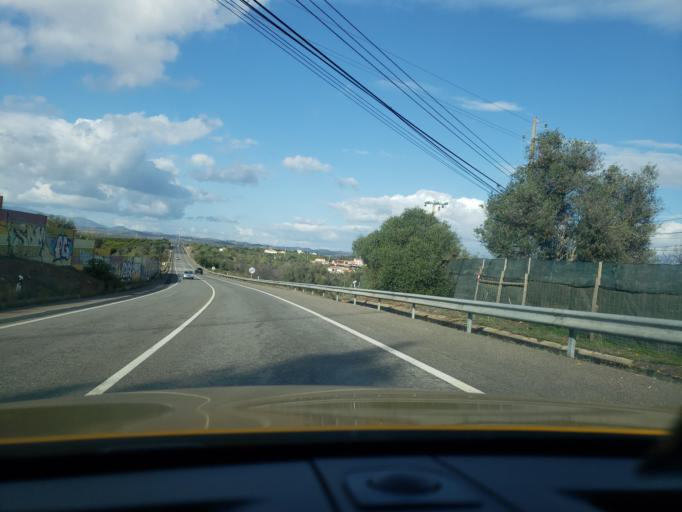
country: PT
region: Faro
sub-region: Silves
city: Silves
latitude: 37.1684
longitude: -8.4425
